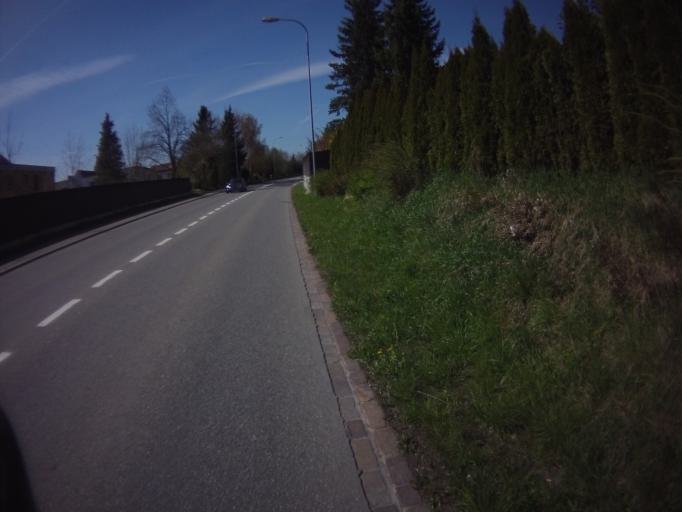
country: CH
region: Aargau
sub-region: Bezirk Bremgarten
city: Rudolfstetten
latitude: 47.3701
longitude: 8.3592
